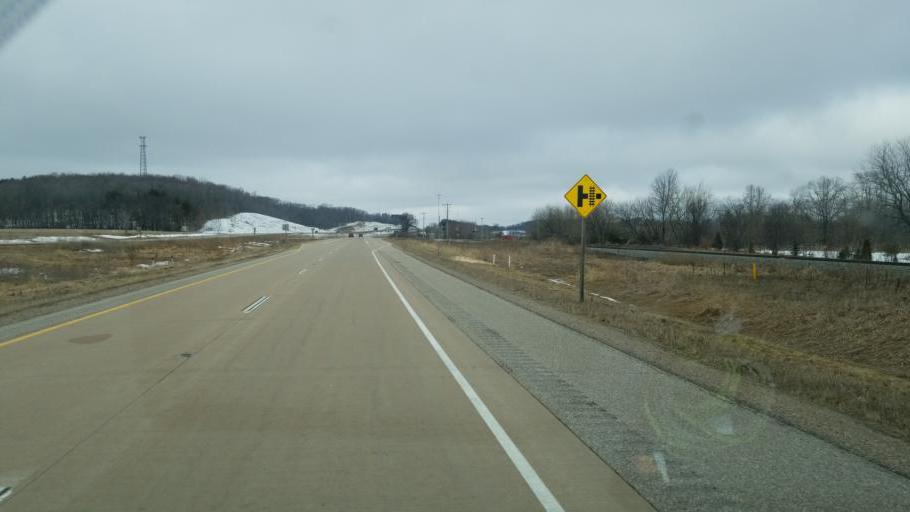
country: US
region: Wisconsin
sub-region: Portage County
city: Amherst
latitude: 44.4078
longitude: -89.2319
